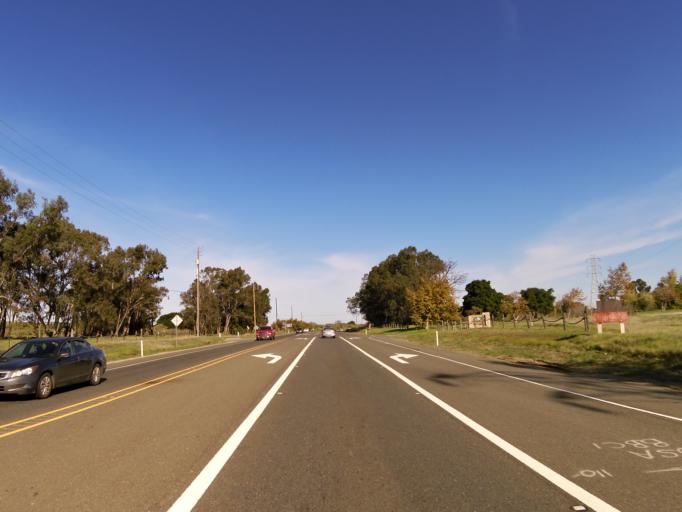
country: US
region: California
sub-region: Solano County
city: Rio Vista
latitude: 38.1097
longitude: -121.6989
